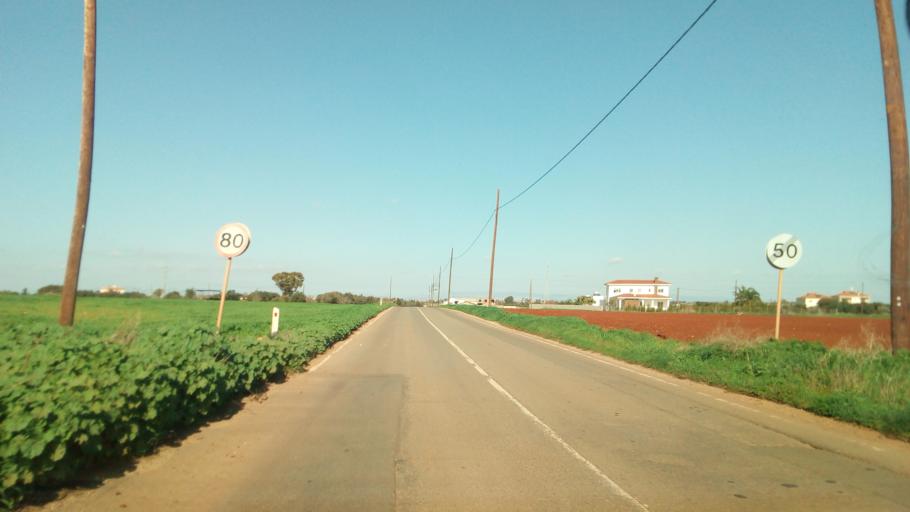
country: CY
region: Ammochostos
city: Avgorou
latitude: 34.9916
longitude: 33.8467
